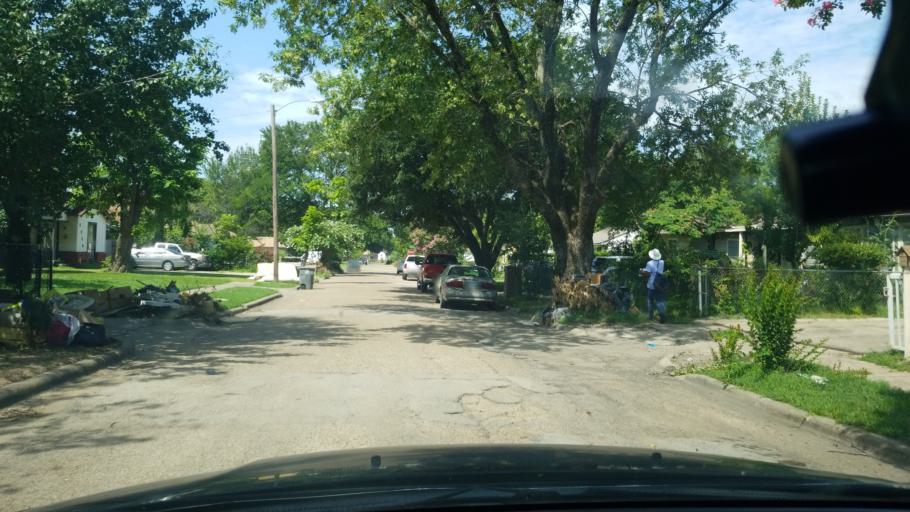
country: US
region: Texas
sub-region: Dallas County
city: Balch Springs
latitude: 32.7401
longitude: -96.6897
